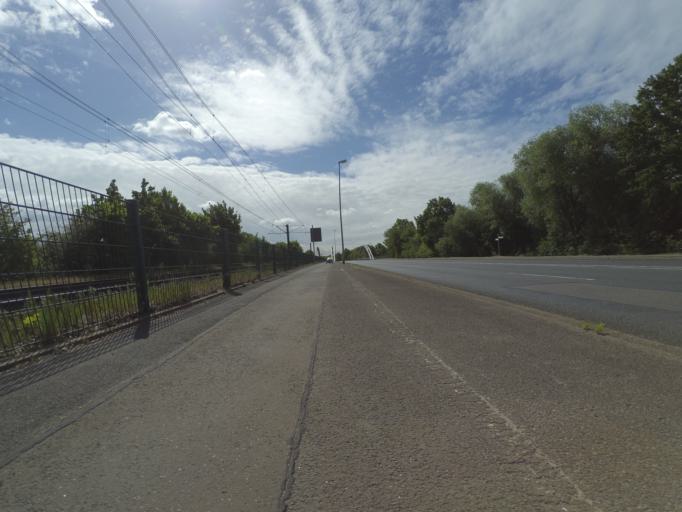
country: DE
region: Lower Saxony
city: Auf der Horst
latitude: 52.4172
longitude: 9.6177
